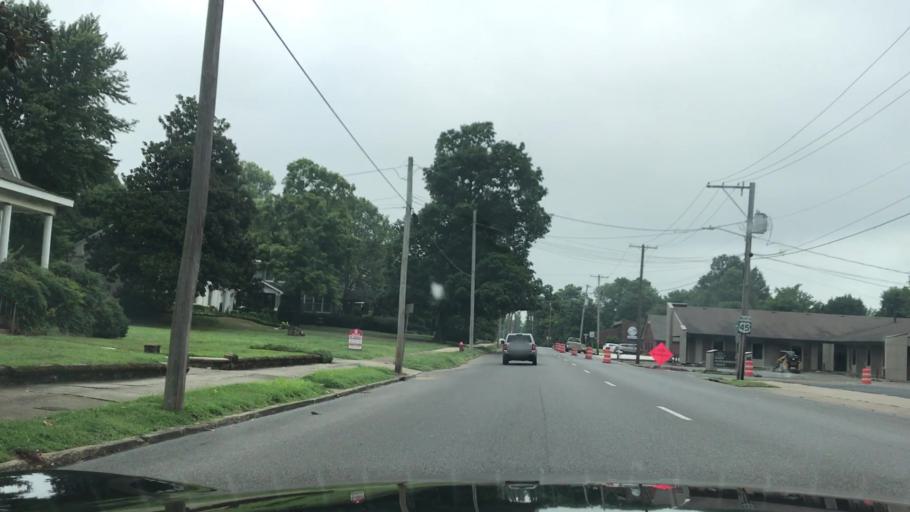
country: US
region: Kentucky
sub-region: Graves County
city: Mayfield
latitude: 36.7438
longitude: -88.6358
